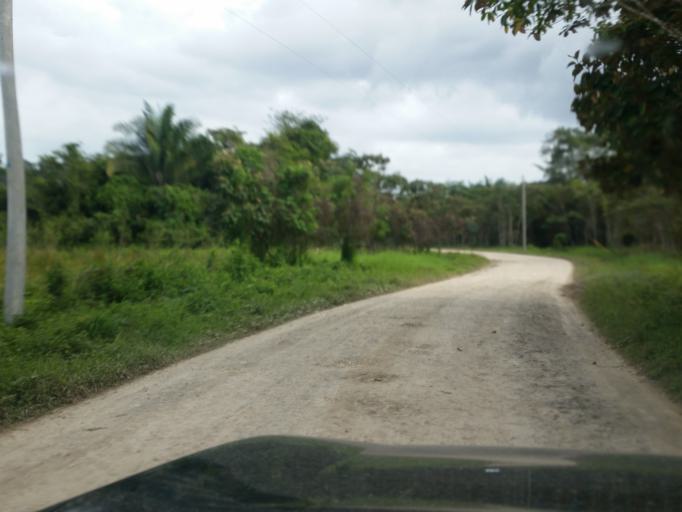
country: CR
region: Alajuela
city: Los Chiles
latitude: 11.1219
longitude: -84.6046
